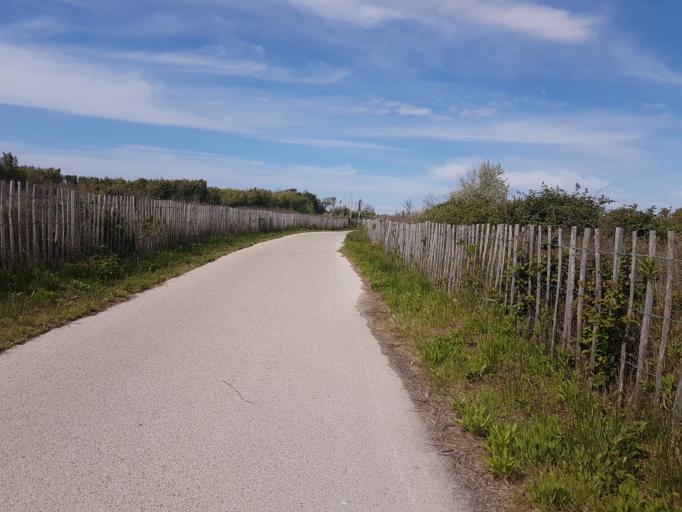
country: FR
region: Languedoc-Roussillon
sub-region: Departement de l'Herault
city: Perols
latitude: 43.5548
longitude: 4.0107
